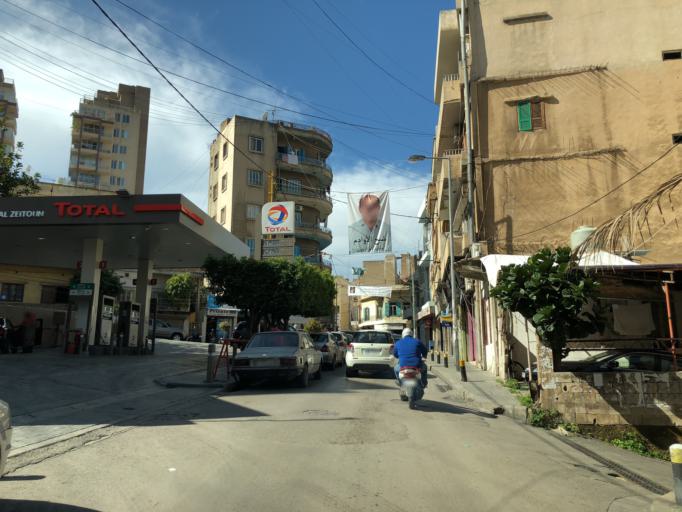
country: LB
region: Beyrouth
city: Beirut
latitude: 33.8877
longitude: 35.5291
